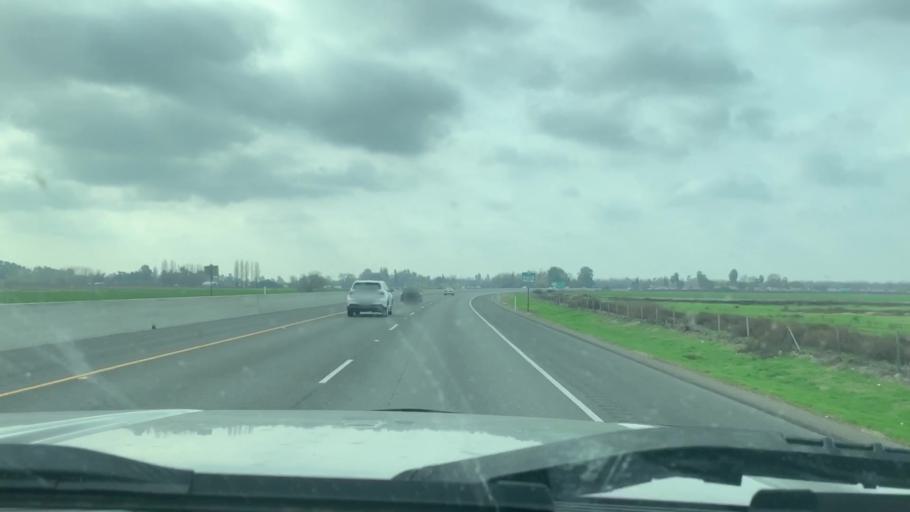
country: US
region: California
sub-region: Kings County
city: Lemoore
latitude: 36.2937
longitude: -119.7635
